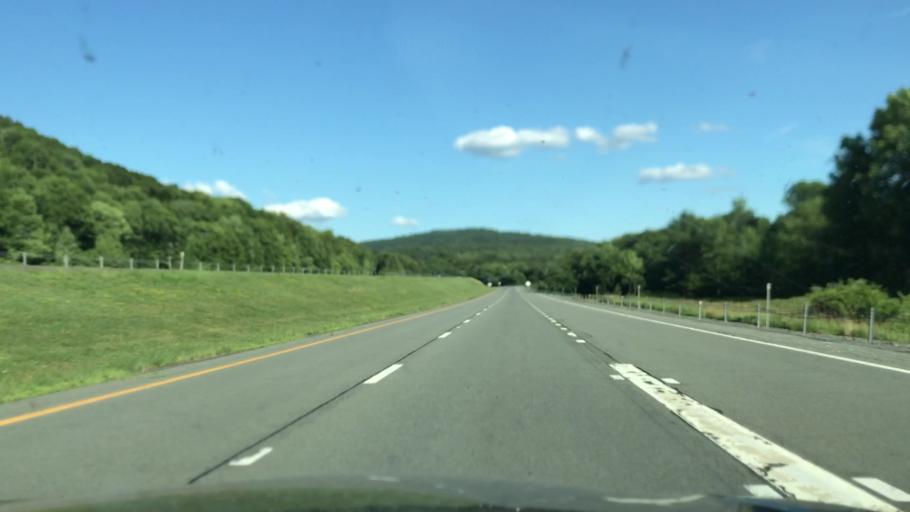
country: US
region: New York
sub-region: Sullivan County
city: Livingston Manor
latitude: 41.9559
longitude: -74.9866
